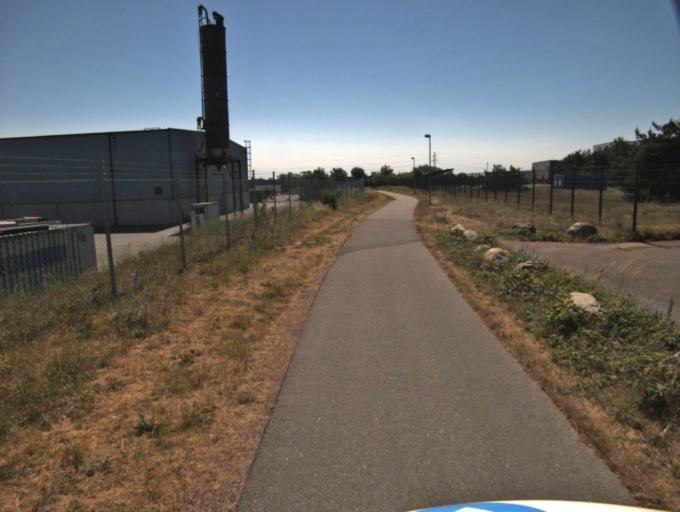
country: SE
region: Skane
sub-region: Kristianstads Kommun
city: Ahus
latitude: 55.9329
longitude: 14.2794
